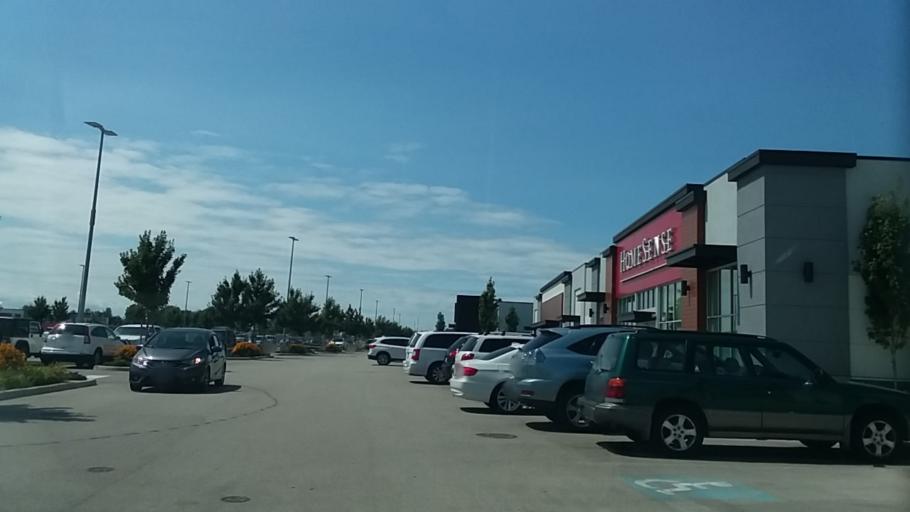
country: CA
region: British Columbia
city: Ladner
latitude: 49.0424
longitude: -123.0855
